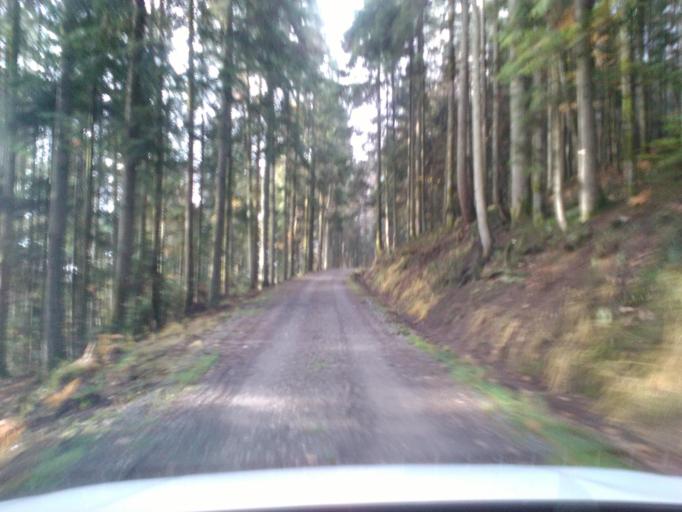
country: FR
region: Lorraine
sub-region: Departement des Vosges
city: Senones
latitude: 48.4172
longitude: 6.9847
